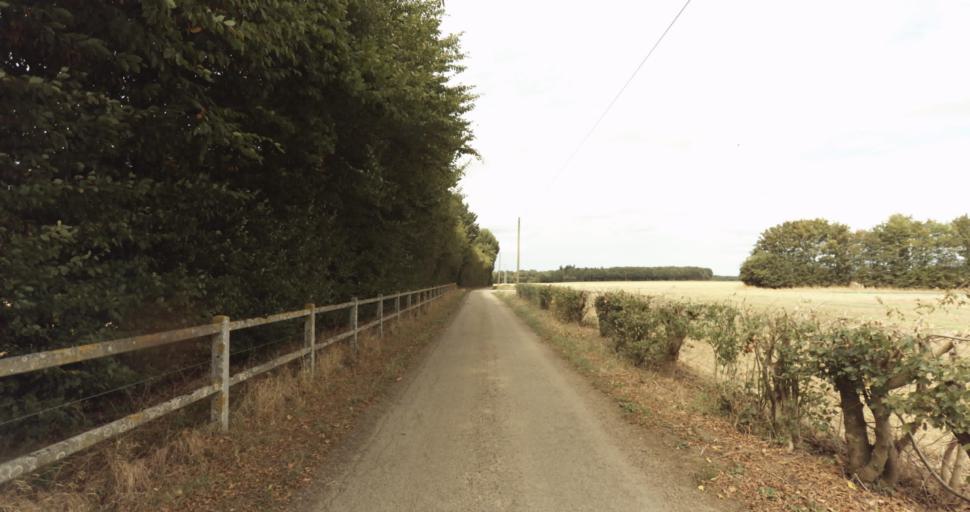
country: FR
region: Lower Normandy
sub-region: Departement de l'Orne
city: Gace
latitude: 48.8898
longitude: 0.3632
